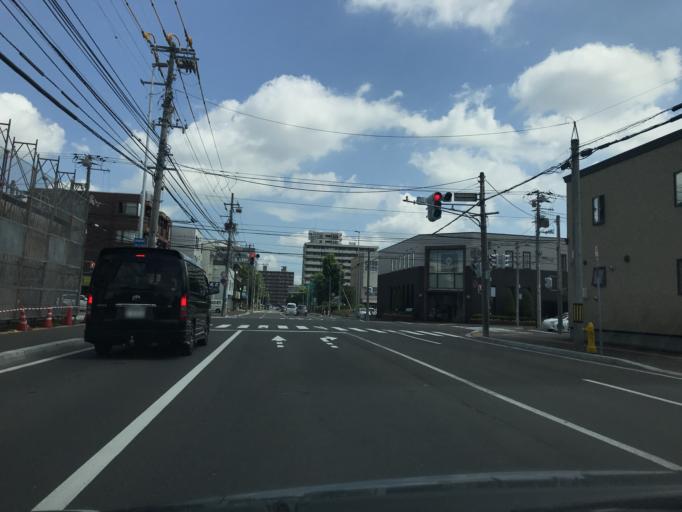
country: JP
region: Hokkaido
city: Sapporo
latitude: 43.0578
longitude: 141.3773
